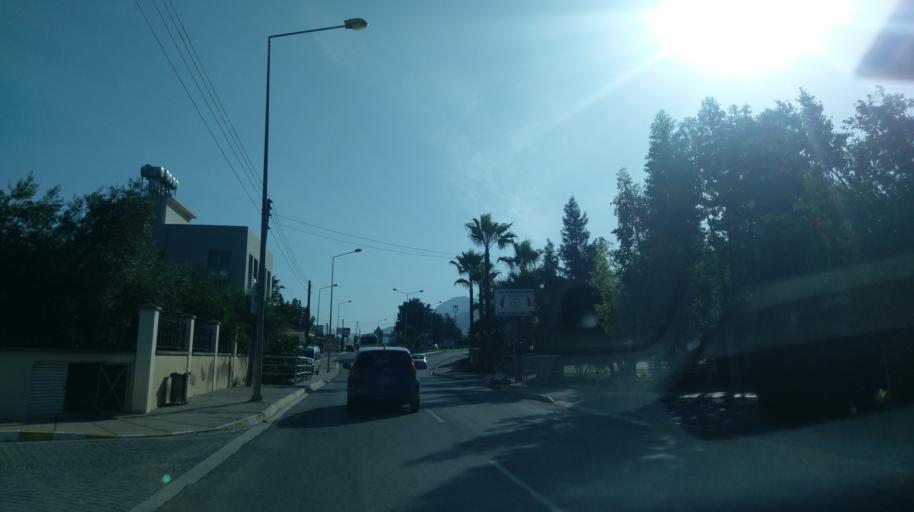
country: CY
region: Keryneia
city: Kyrenia
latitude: 35.3257
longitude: 33.3420
